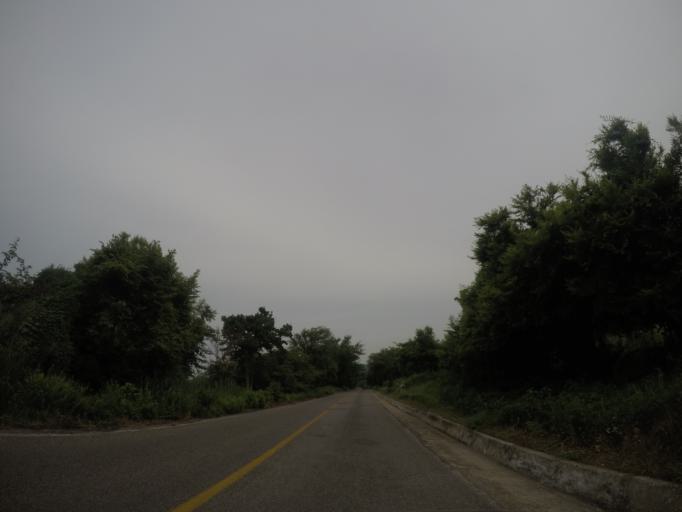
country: MX
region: Oaxaca
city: San Pedro Mixtepec
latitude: 15.9484
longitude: -97.1896
